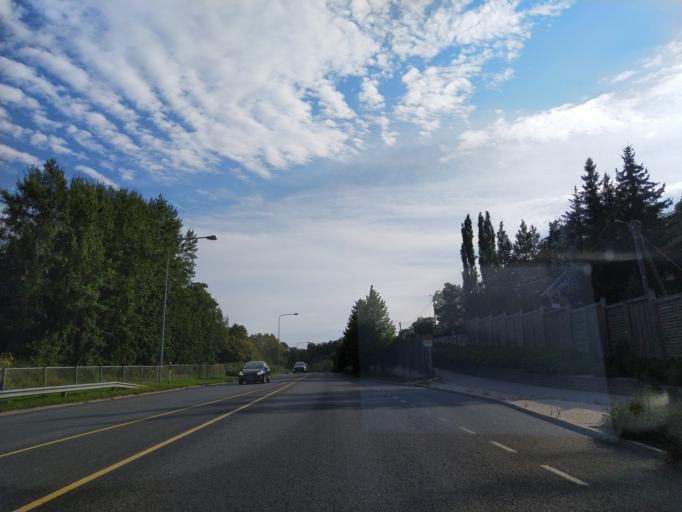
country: FI
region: Varsinais-Suomi
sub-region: Turku
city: Turku
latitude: 60.4206
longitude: 22.2331
